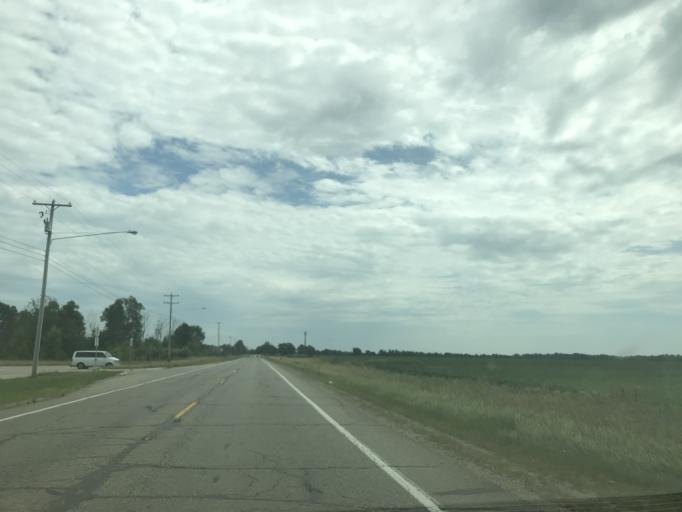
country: US
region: Michigan
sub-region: Clinton County
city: Wacousta
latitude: 42.7967
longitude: -84.7331
